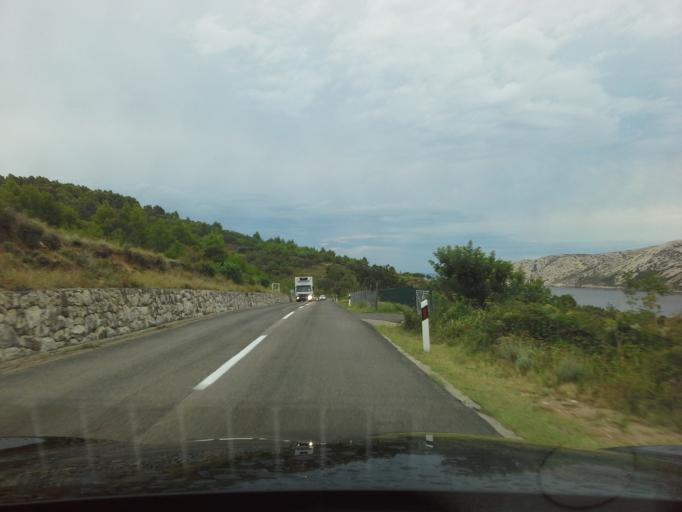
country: HR
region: Primorsko-Goranska
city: Banjol
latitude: 44.7159
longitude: 14.8259
